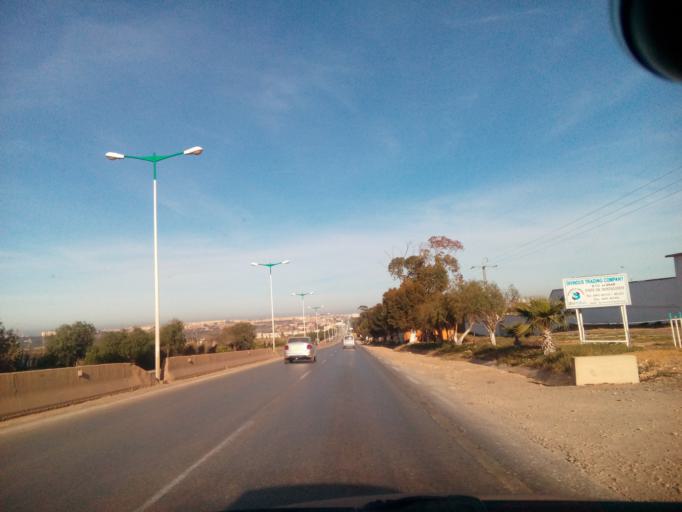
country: DZ
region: Mostaganem
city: Mostaganem
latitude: 35.8942
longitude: 0.1278
